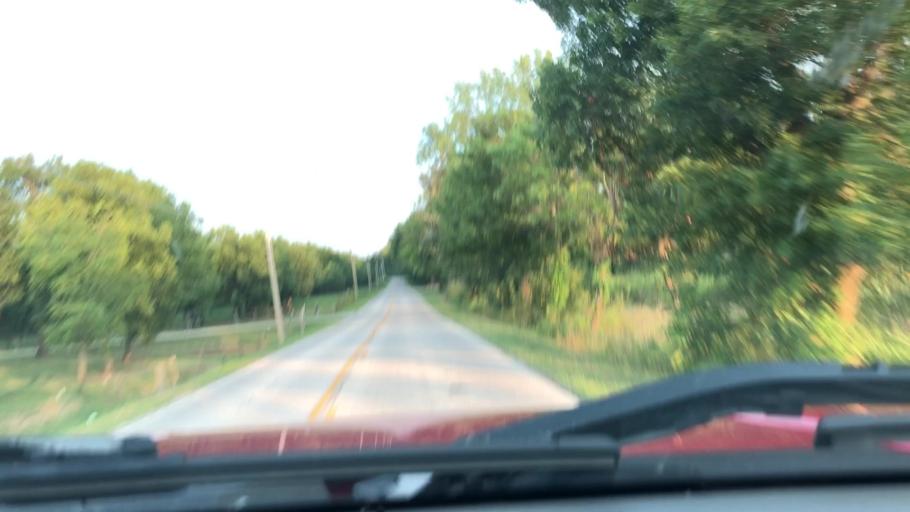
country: US
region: Missouri
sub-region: Jasper County
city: Joplin
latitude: 37.0204
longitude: -94.5102
